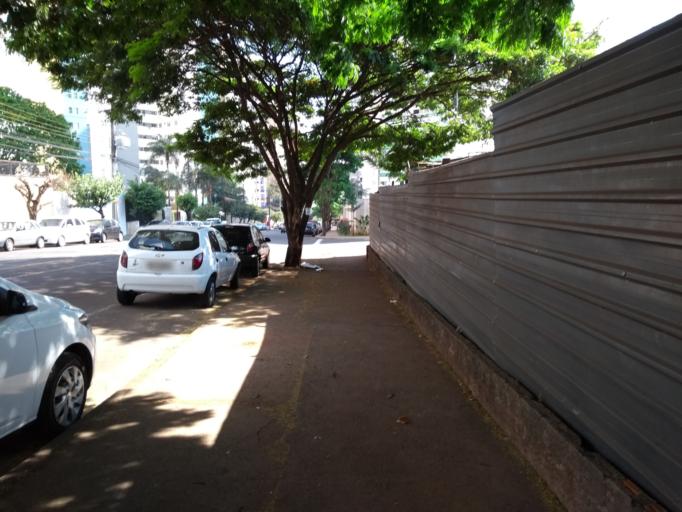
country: BR
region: Parana
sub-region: Londrina
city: Londrina
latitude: -23.3341
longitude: -51.1745
